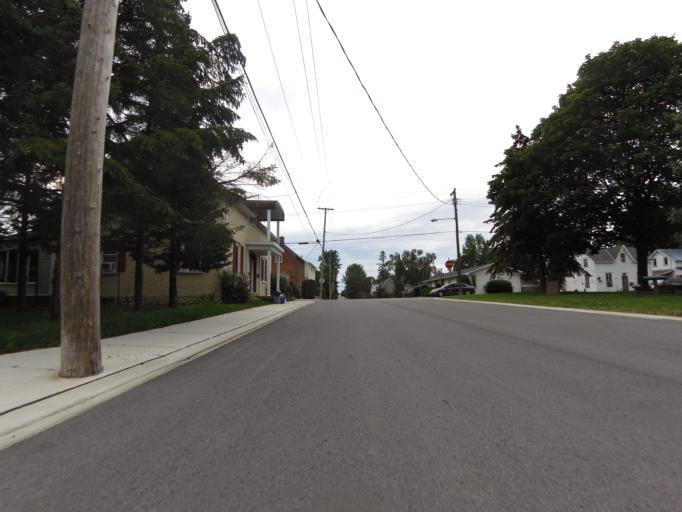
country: CA
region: Ontario
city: Carleton Place
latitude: 45.1409
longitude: -76.1504
